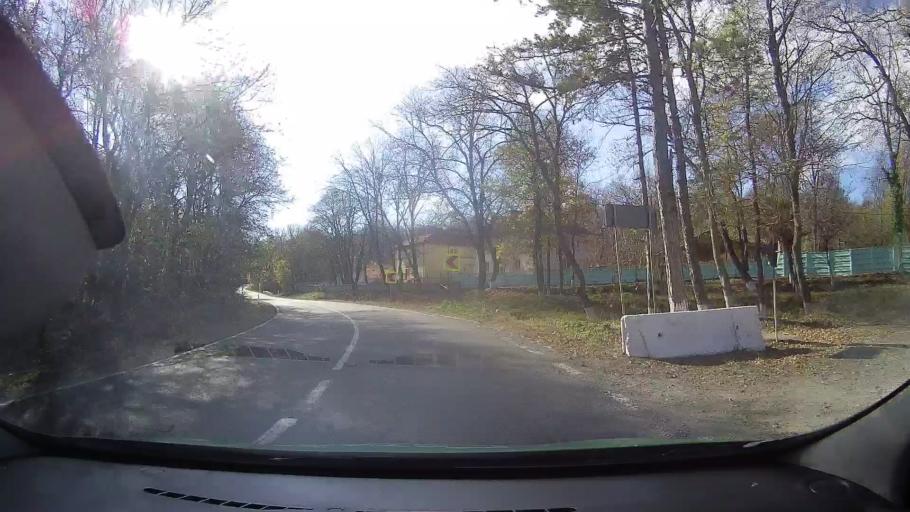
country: RO
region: Tulcea
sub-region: Oras Babadag
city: Babadag
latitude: 44.8442
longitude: 28.6978
